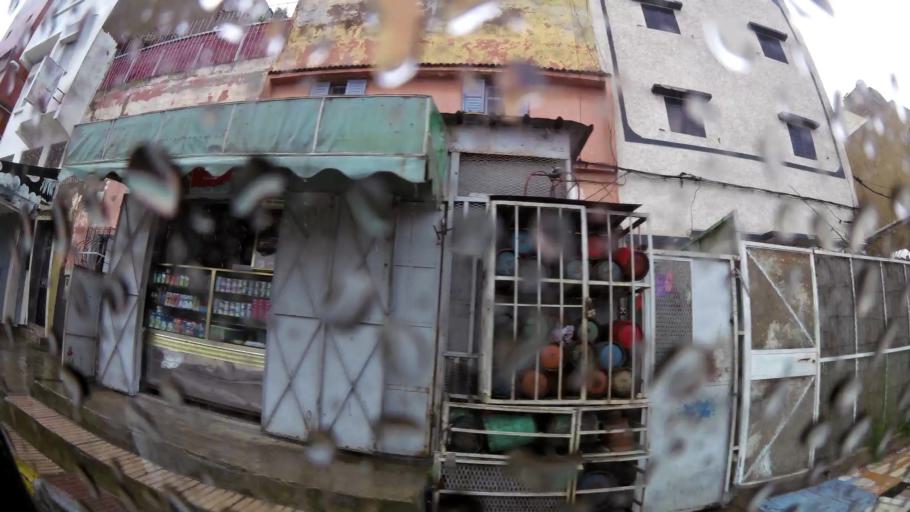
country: MA
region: Grand Casablanca
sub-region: Mediouna
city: Tit Mellil
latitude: 33.5539
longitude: -7.5508
